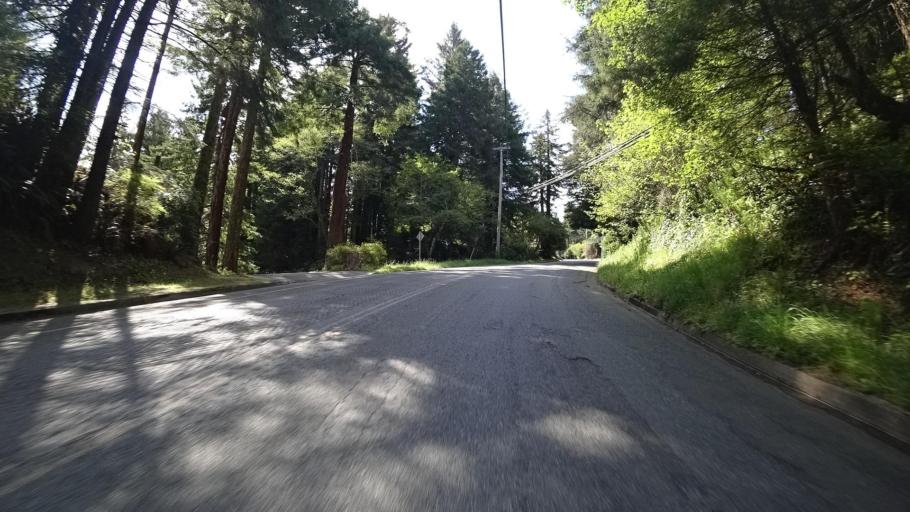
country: US
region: California
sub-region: Humboldt County
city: Cutten
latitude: 40.7662
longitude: -124.1546
